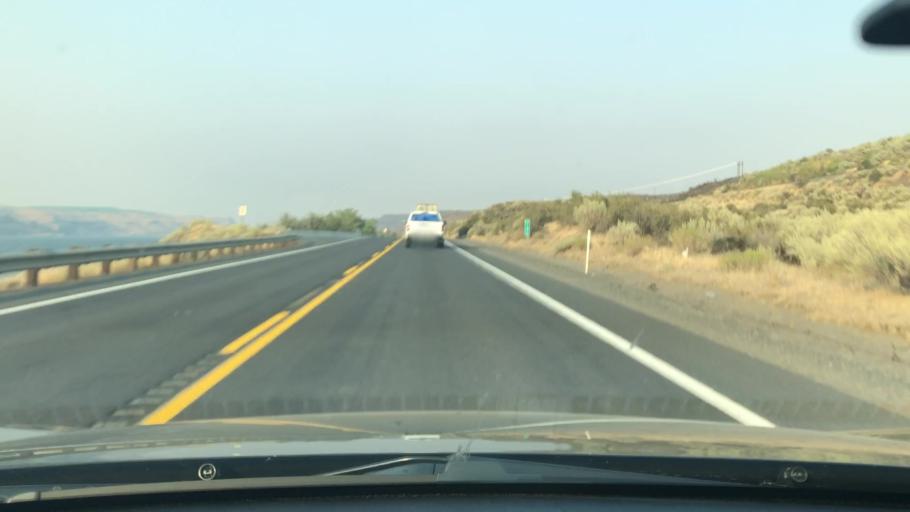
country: US
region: Oregon
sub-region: Umatilla County
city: Stanfield
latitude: 45.9268
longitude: -119.1068
